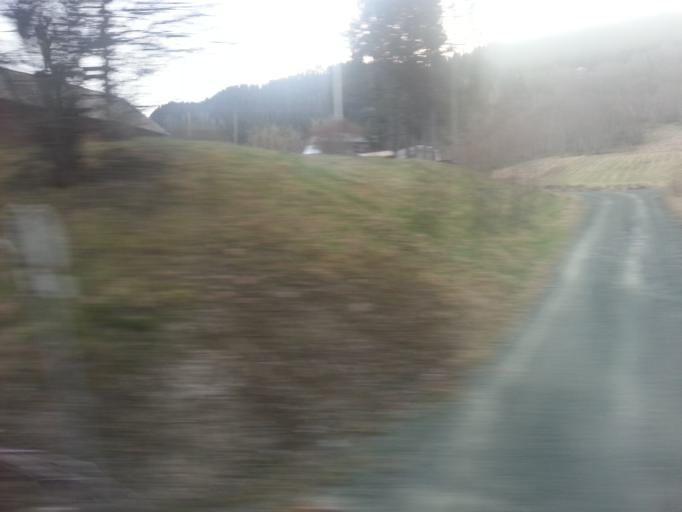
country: NO
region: Sor-Trondelag
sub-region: Melhus
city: Melhus
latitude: 63.2269
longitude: 10.2894
